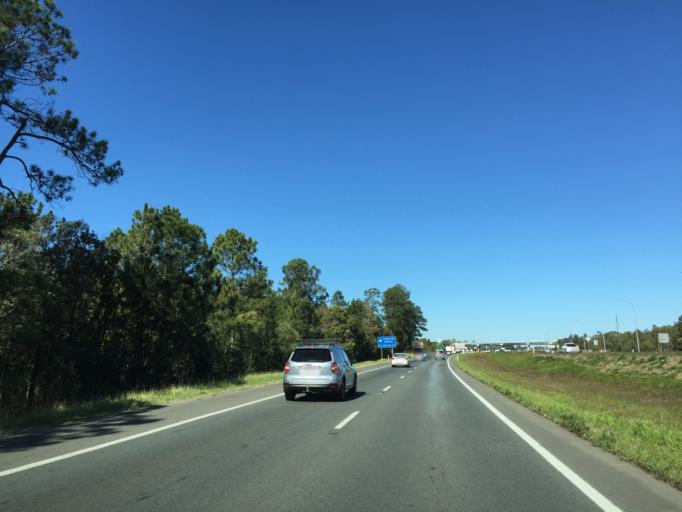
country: AU
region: Queensland
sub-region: Moreton Bay
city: Caboolture
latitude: -27.0656
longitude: 152.9777
